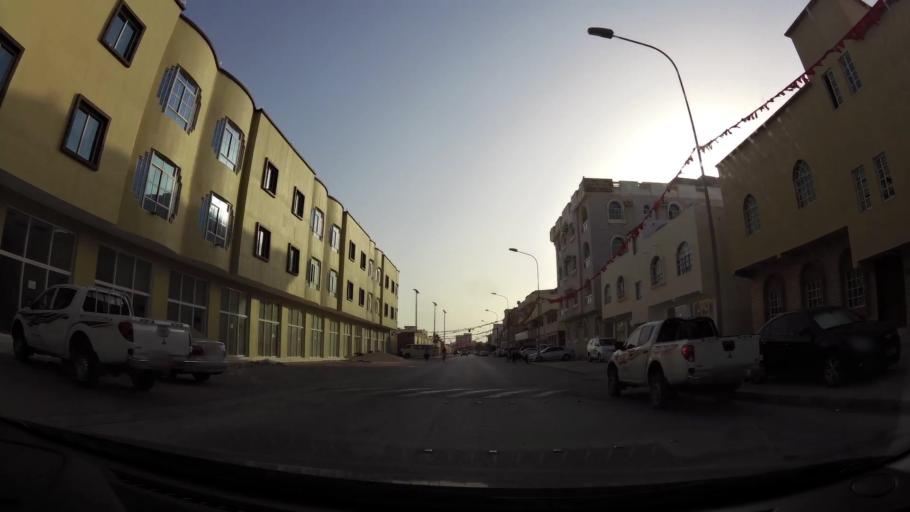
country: OM
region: Zufar
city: Salalah
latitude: 17.0150
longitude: 54.0993
